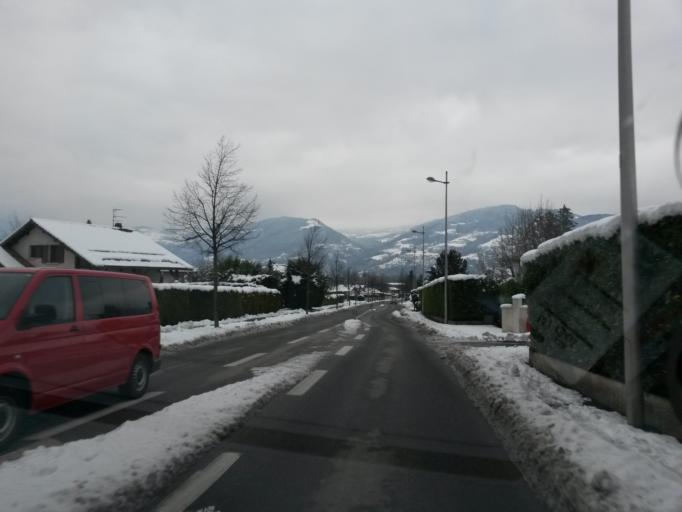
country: FR
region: Rhone-Alpes
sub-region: Departement de l'Isere
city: Crolles
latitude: 45.2755
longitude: 5.8771
